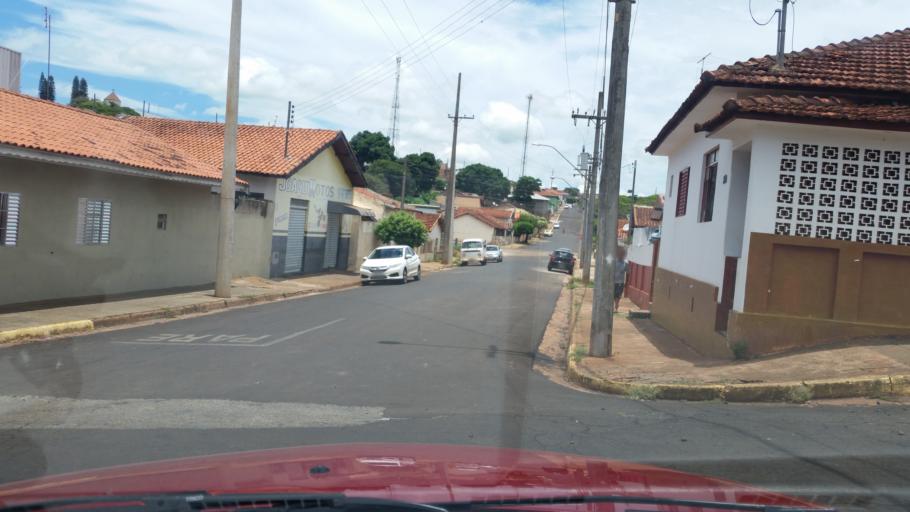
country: BR
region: Sao Paulo
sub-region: Itai
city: Itai
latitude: -23.4155
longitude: -49.0927
